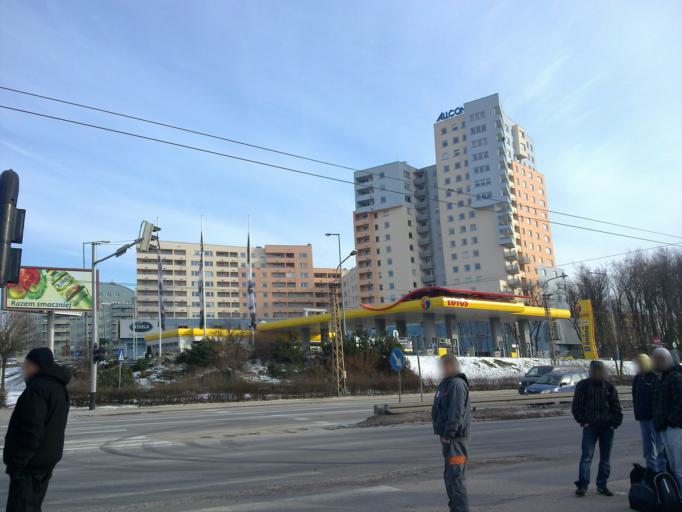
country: PL
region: Pomeranian Voivodeship
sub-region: Gdynia
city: Gdynia
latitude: 54.4969
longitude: 18.5381
